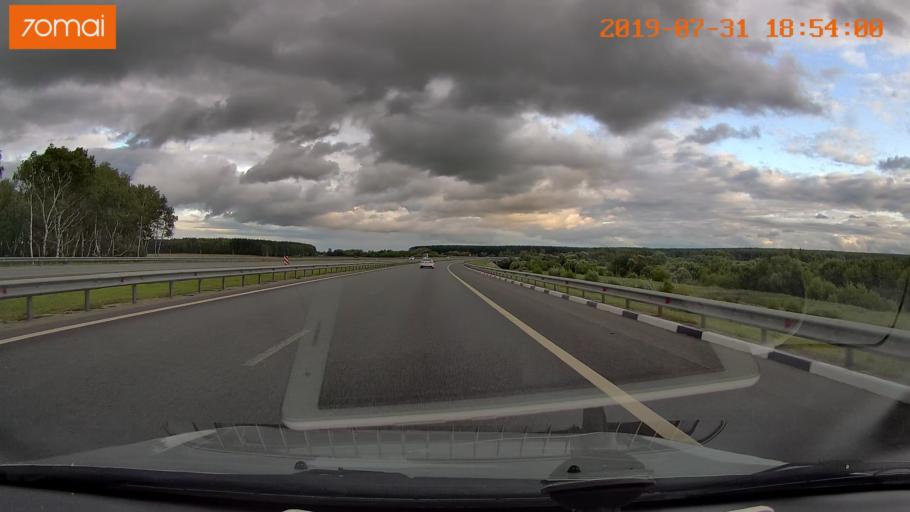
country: RU
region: Moskovskaya
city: Raduzhnyy
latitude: 55.1954
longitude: 38.6652
